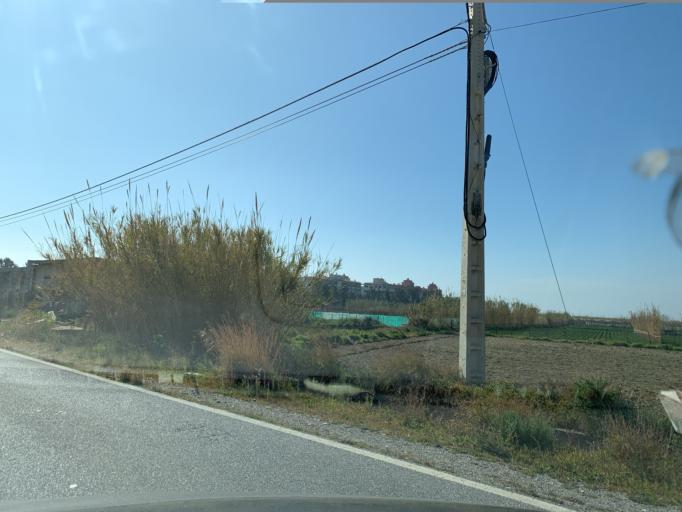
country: ES
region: Andalusia
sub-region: Provincia de Granada
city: Salobrena
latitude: 36.7252
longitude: -3.5591
